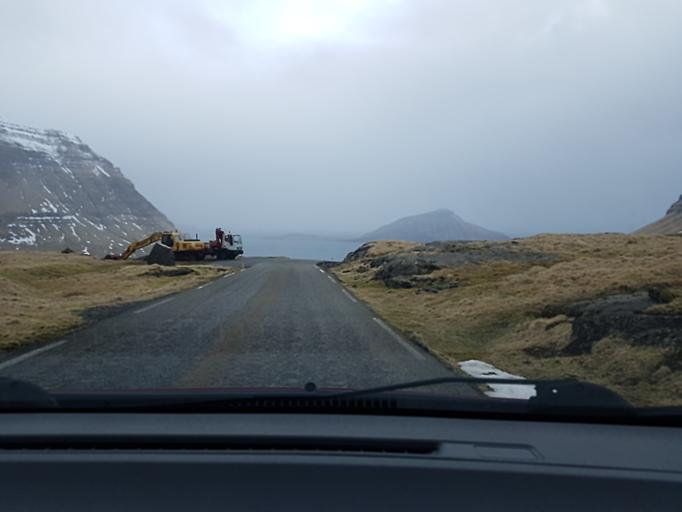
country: FO
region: Streymoy
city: Kollafjordhur
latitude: 62.0513
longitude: -6.9221
